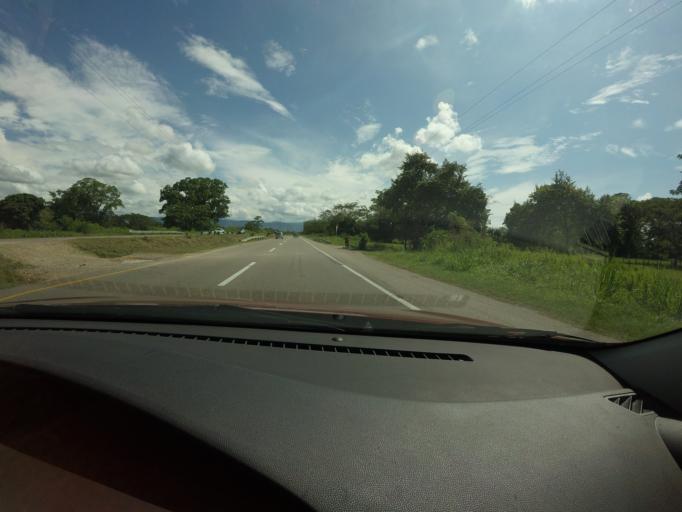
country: CO
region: Antioquia
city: Puerto Triunfo
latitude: 5.6955
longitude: -74.6137
